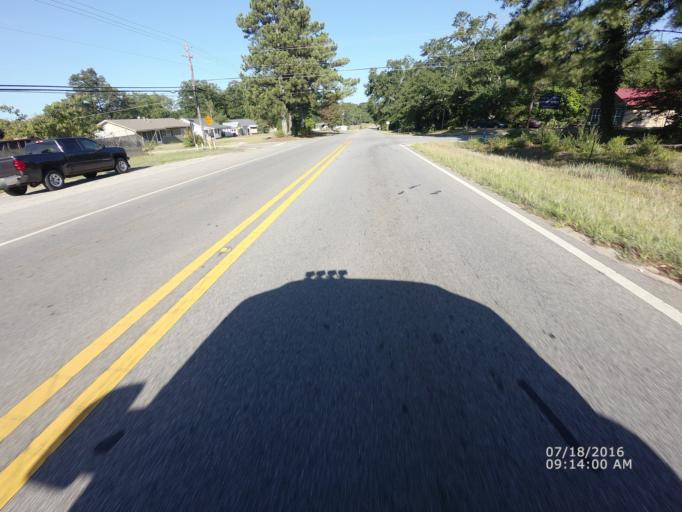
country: US
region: Alabama
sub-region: Chambers County
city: Huguley
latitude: 32.8464
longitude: -85.2368
